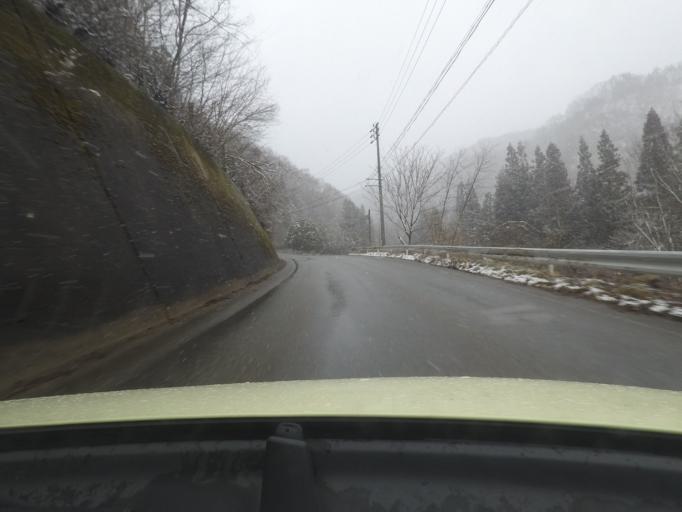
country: JP
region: Gifu
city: Takayama
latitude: 36.1328
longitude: 137.3201
